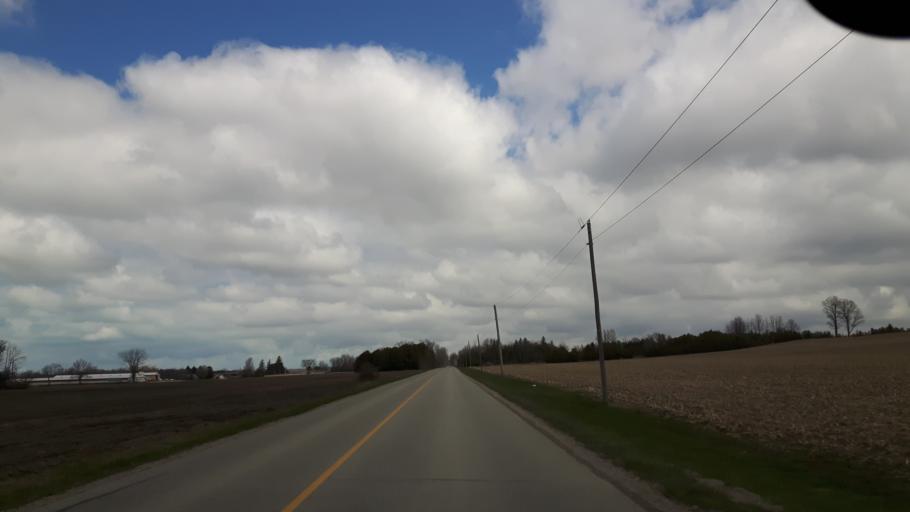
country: CA
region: Ontario
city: Goderich
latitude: 43.6801
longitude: -81.6847
